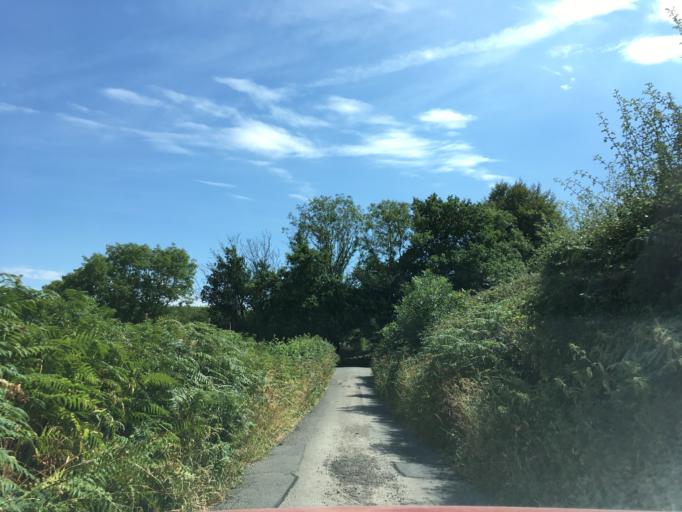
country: GB
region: Wales
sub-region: Caerphilly County Borough
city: Risca
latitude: 51.5967
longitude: -3.0963
